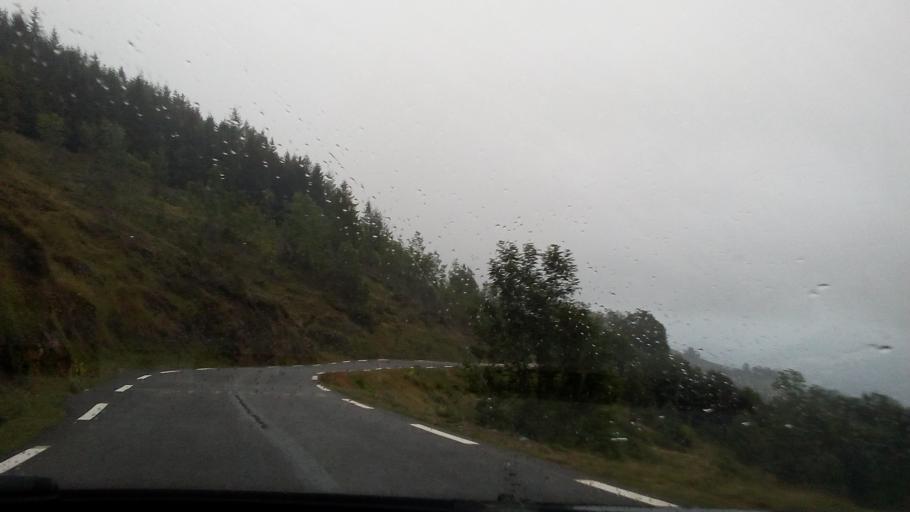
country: FR
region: Midi-Pyrenees
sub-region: Departement des Hautes-Pyrenees
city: Cauterets
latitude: 42.9603
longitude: -0.2485
